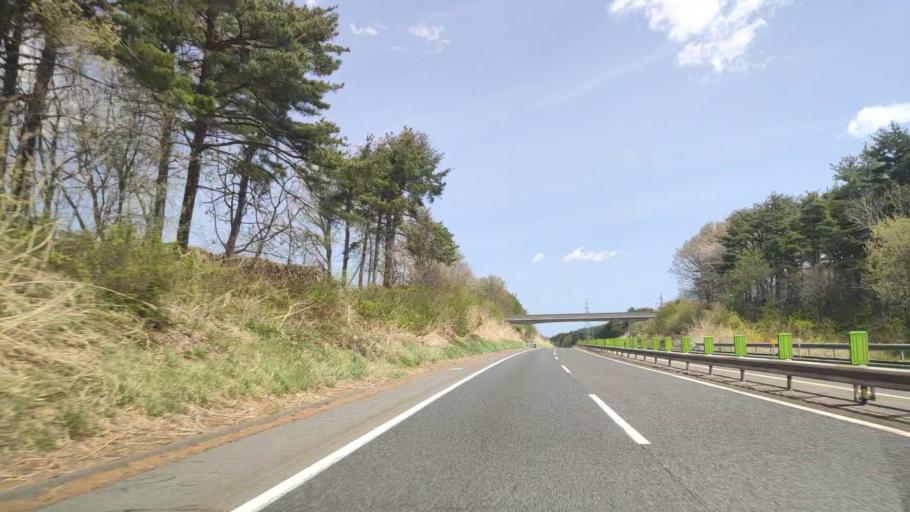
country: JP
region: Aomori
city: Hachinohe
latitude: 40.4306
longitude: 141.4417
